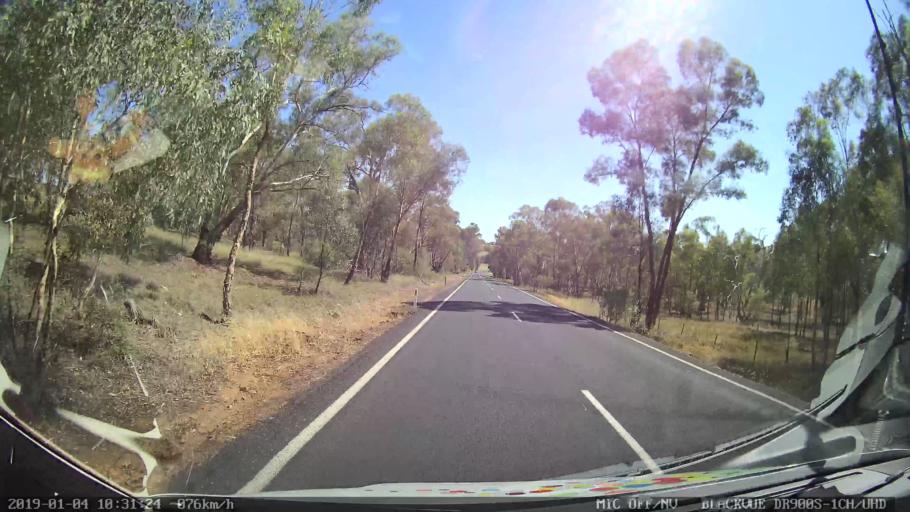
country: AU
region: New South Wales
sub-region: Cabonne
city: Canowindra
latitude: -33.3352
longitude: 148.6322
